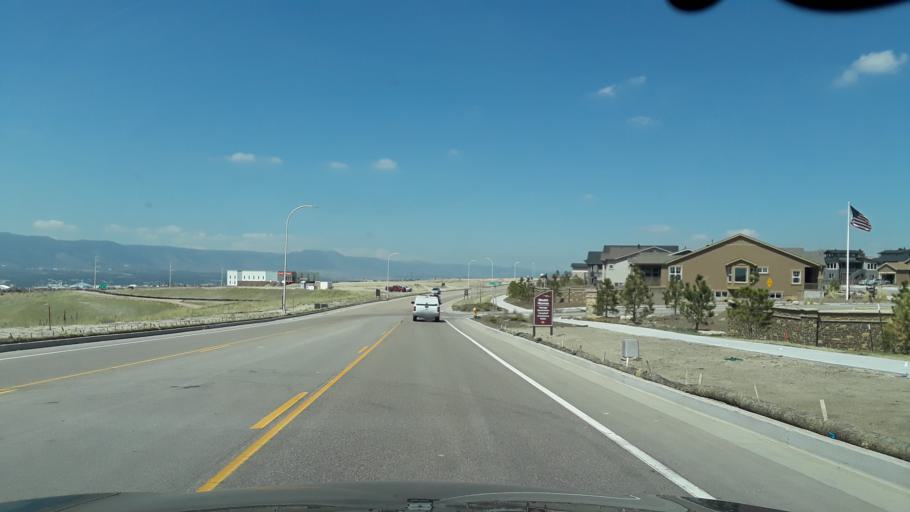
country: US
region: Colorado
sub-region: El Paso County
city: Black Forest
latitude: 38.9801
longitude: -104.7547
